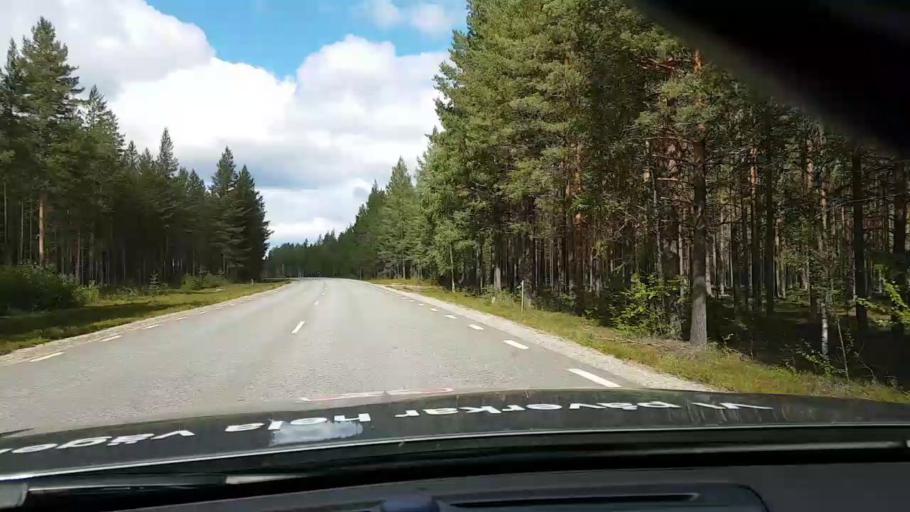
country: SE
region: Vaesternorrland
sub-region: OErnskoeldsviks Kommun
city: Bredbyn
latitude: 63.5347
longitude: 17.9661
